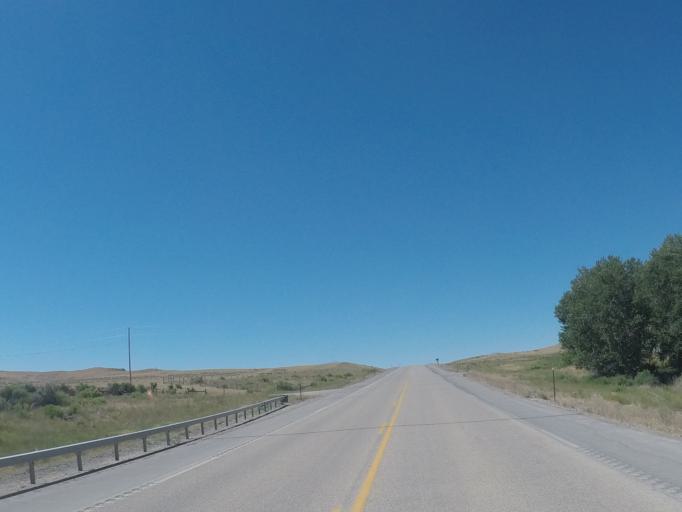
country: US
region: Wyoming
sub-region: Big Horn County
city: Greybull
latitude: 44.5253
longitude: -107.8322
